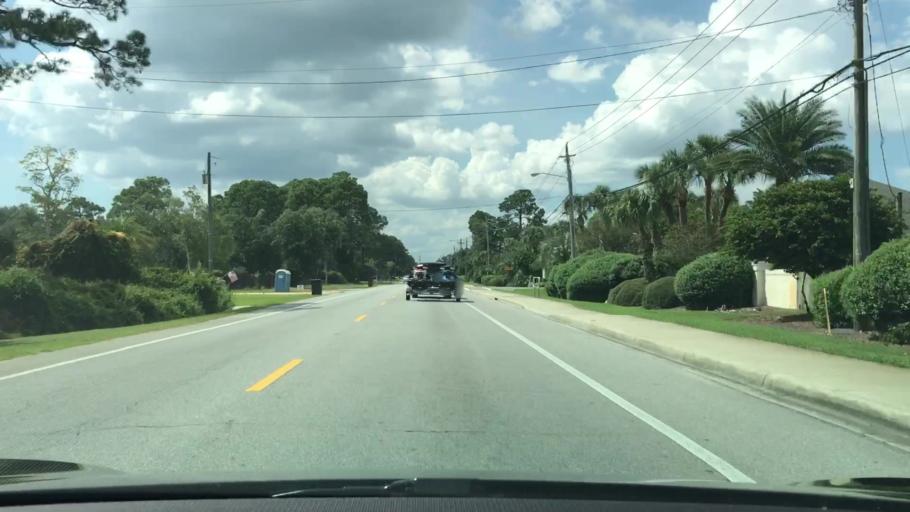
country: US
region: Florida
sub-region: Bay County
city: Lower Grand Lagoon
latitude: 30.1650
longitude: -85.7744
